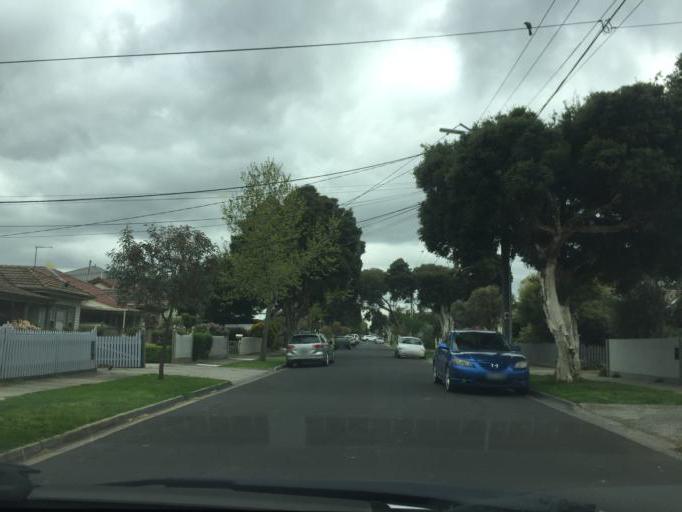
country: AU
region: Victoria
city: Spotswood
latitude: -37.8215
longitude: 144.8797
